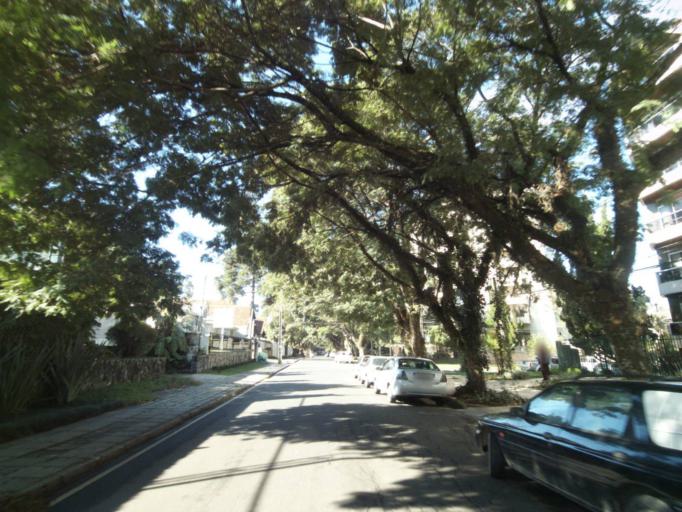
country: BR
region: Parana
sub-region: Curitiba
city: Curitiba
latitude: -25.4087
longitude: -49.2474
